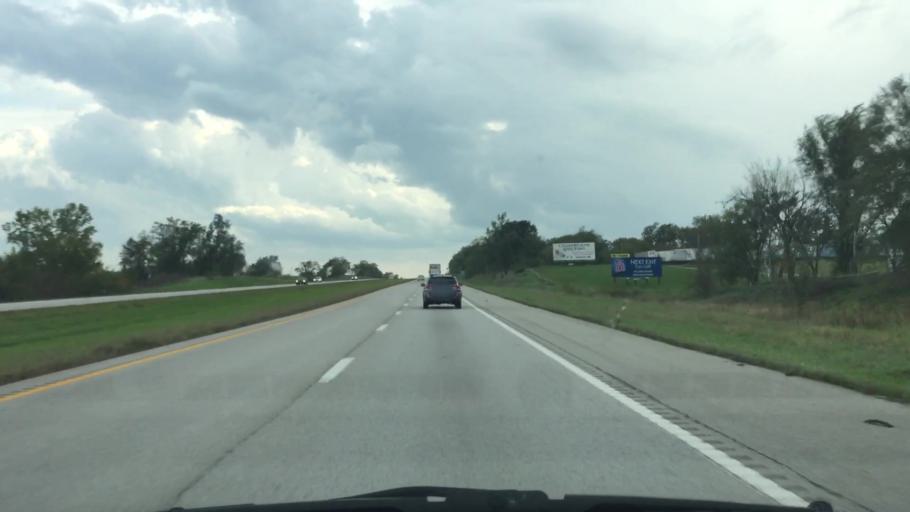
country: US
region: Missouri
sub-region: Clinton County
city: Cameron
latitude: 39.7918
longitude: -94.2044
